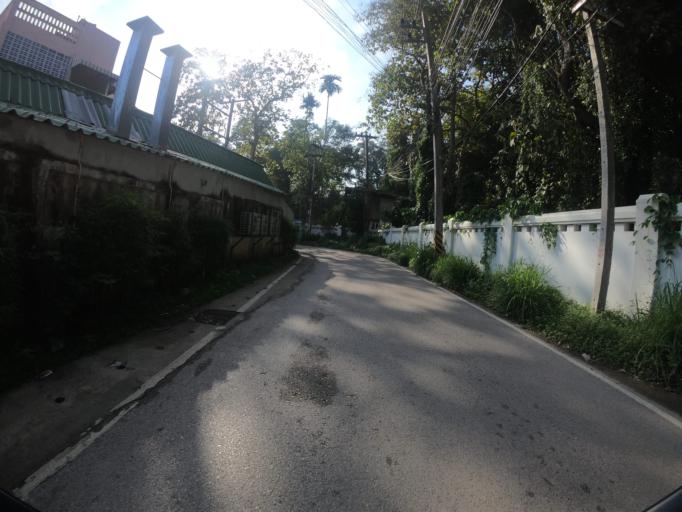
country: TH
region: Chiang Mai
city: Chiang Mai
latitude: 18.8139
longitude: 98.9542
